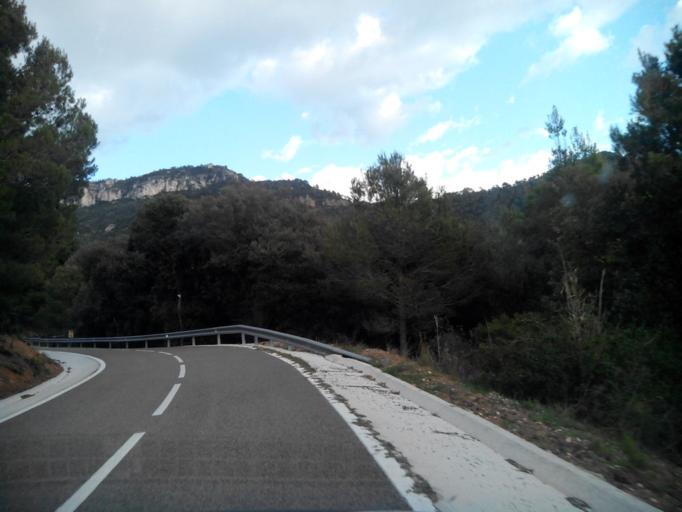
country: ES
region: Catalonia
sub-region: Provincia de Tarragona
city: Vilaplana
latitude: 41.2386
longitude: 1.0431
